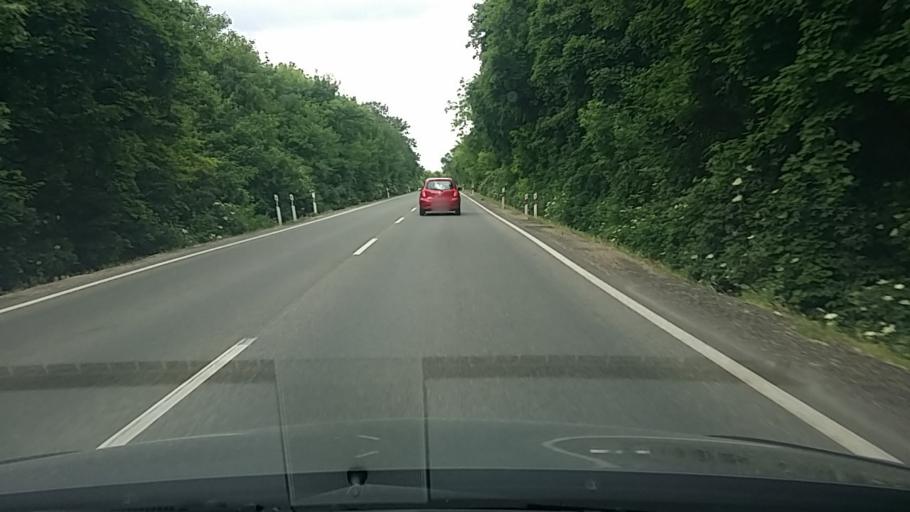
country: HU
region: Fejer
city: dunaujvaros
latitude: 46.9639
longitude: 18.9086
